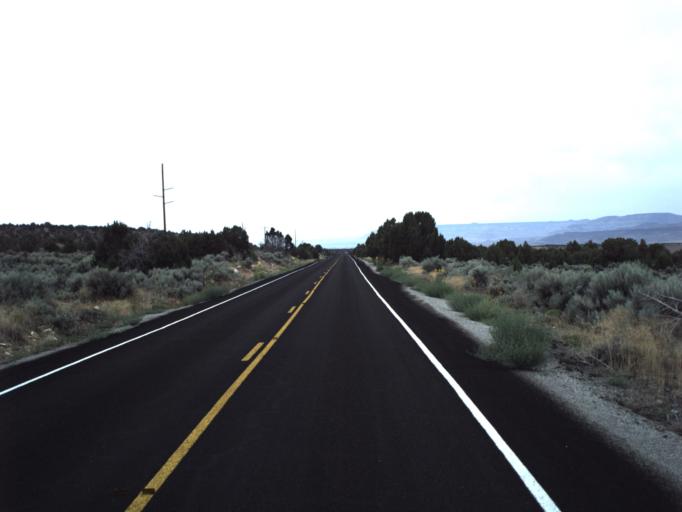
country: US
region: Utah
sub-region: Carbon County
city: East Carbon City
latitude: 39.5041
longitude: -110.3977
